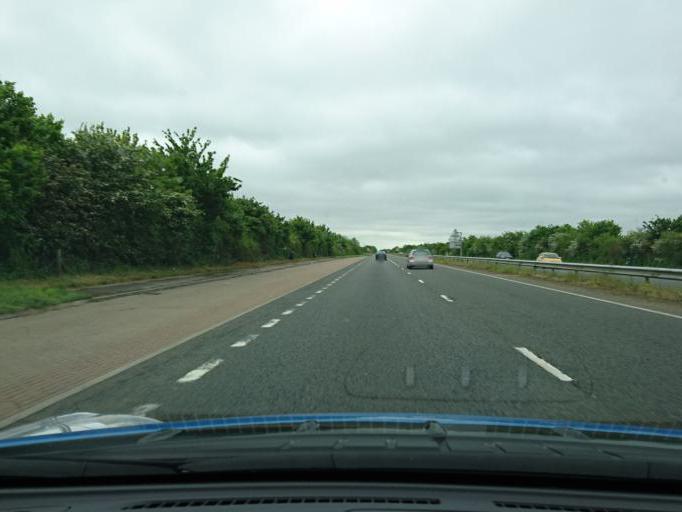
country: GB
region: England
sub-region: Oxfordshire
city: Frilford
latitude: 51.6850
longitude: -1.4055
